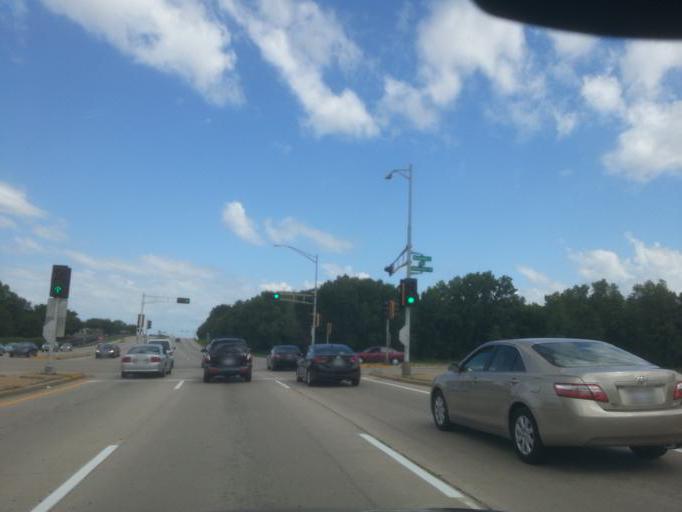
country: US
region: Wisconsin
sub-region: Dane County
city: Monona
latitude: 43.1108
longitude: -89.3179
